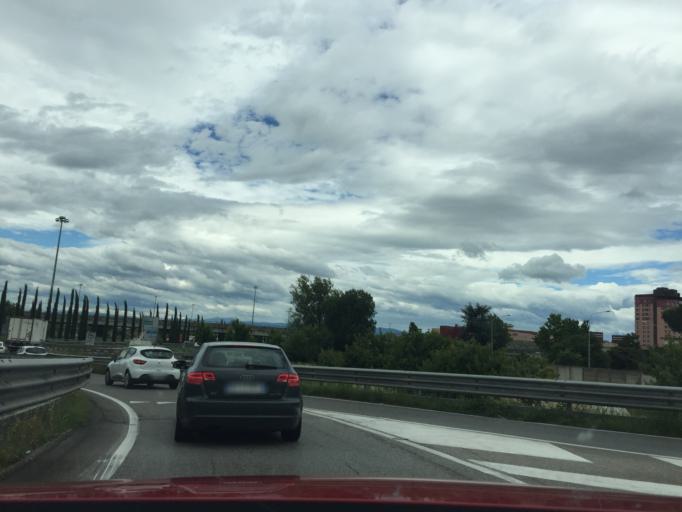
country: IT
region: Tuscany
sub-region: Province of Florence
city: Scandicci
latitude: 43.7691
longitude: 11.1895
